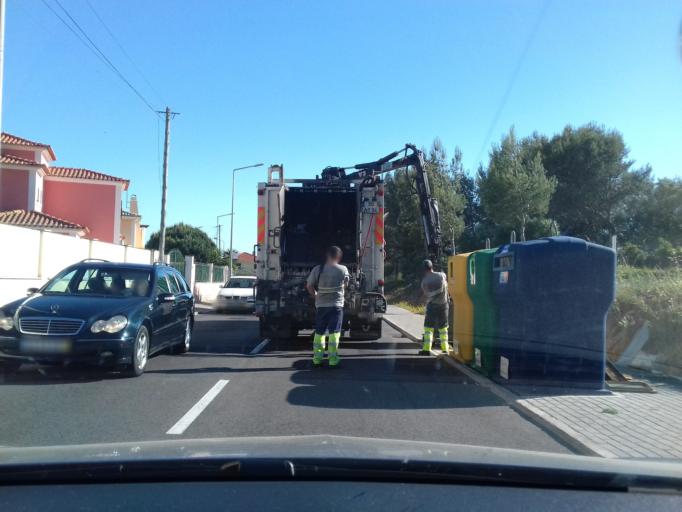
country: PT
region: Lisbon
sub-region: Cascais
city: Alcabideche
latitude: 38.7231
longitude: -9.4130
